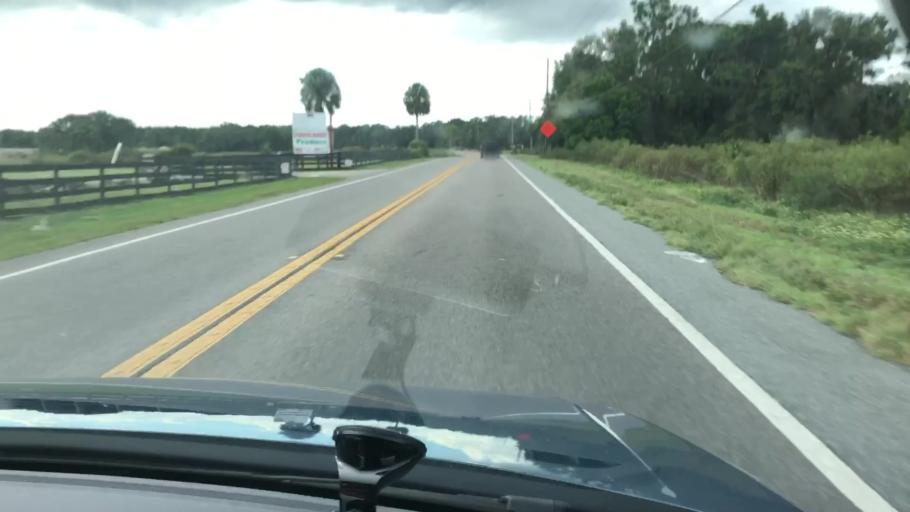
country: US
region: Florida
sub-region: Lake County
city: Mount Plymouth
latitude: 28.8162
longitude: -81.4722
